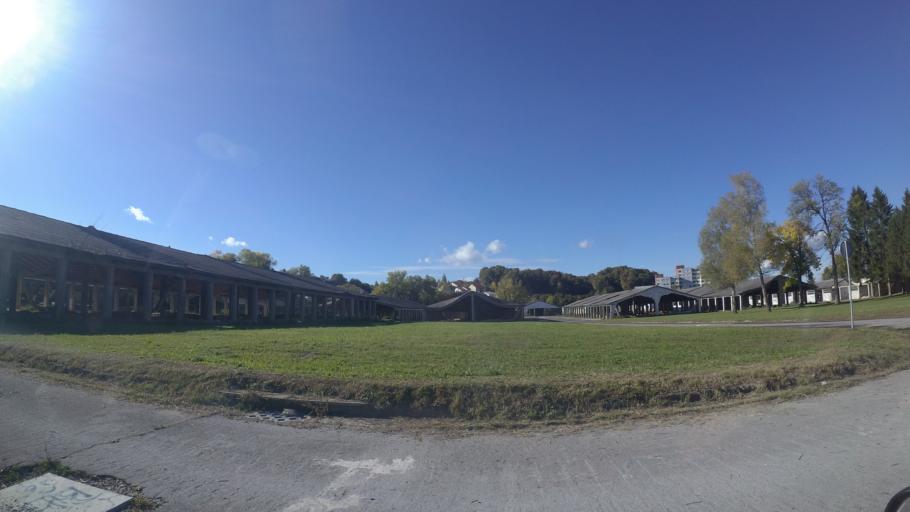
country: HR
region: Karlovacka
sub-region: Grad Karlovac
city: Karlovac
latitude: 45.4834
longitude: 15.5392
